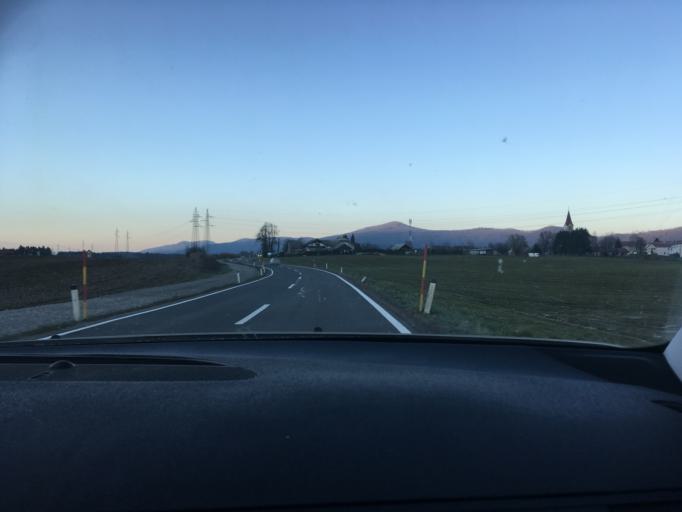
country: SI
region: Kocevje
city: Kocevje
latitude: 45.6646
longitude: 14.8396
